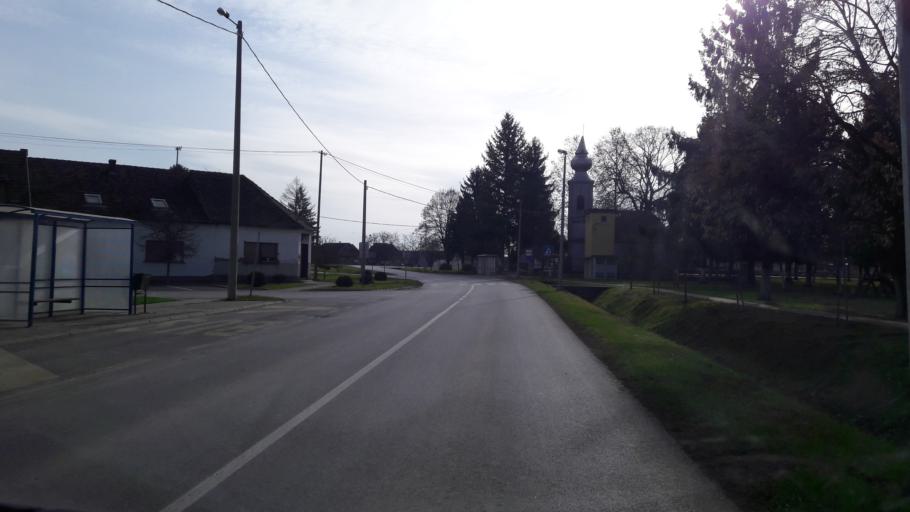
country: HR
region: Osjecko-Baranjska
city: Semeljci
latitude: 45.3526
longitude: 18.5561
